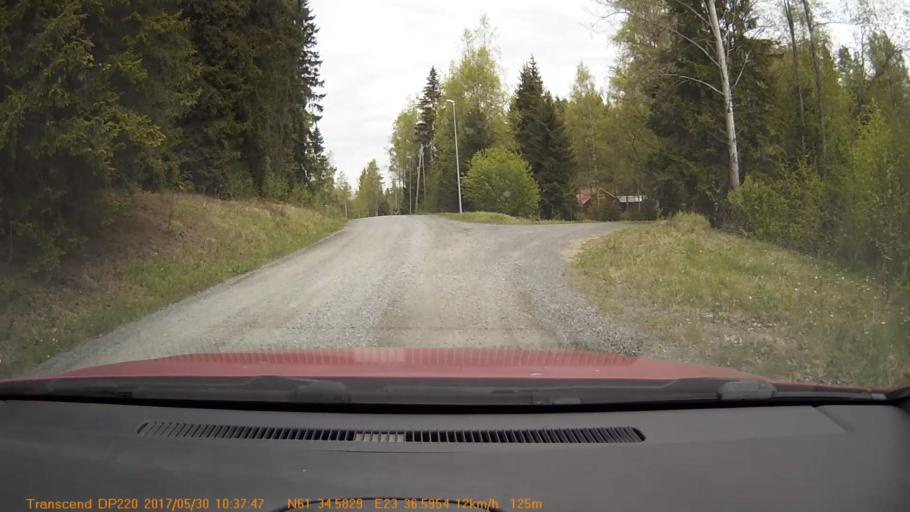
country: FI
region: Pirkanmaa
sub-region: Tampere
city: Yloejaervi
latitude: 61.5764
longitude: 23.6100
